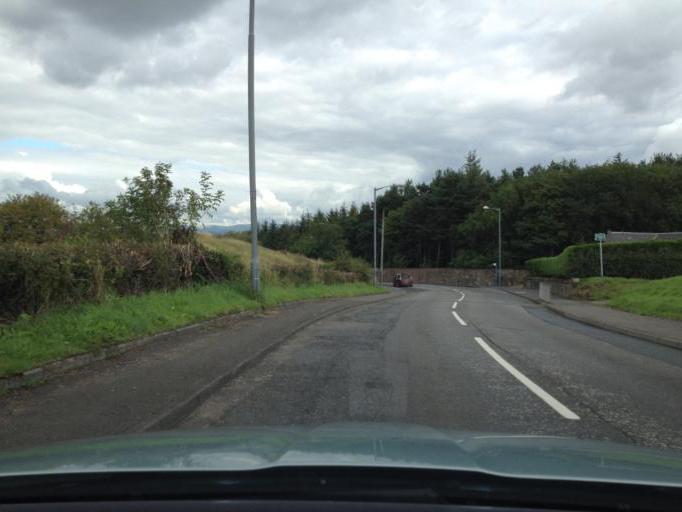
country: GB
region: Scotland
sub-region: Falkirk
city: Falkirk
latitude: 55.9883
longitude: -3.7881
